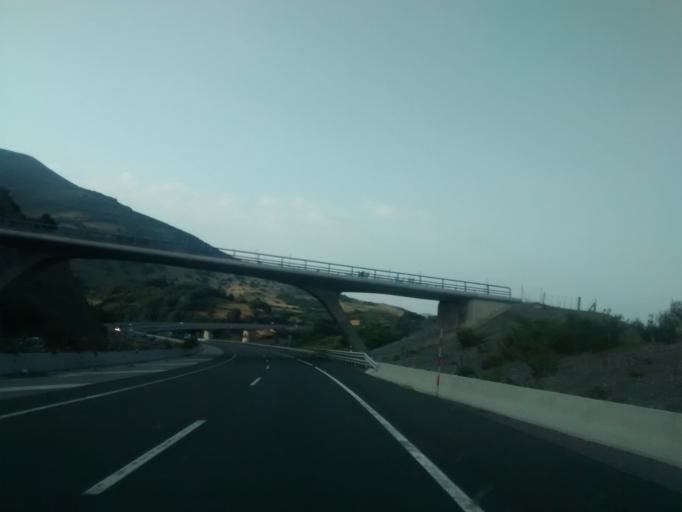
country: ES
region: Cantabria
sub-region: Provincia de Cantabria
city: Barcena de Pie de Concha
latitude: 43.1151
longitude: -4.0828
